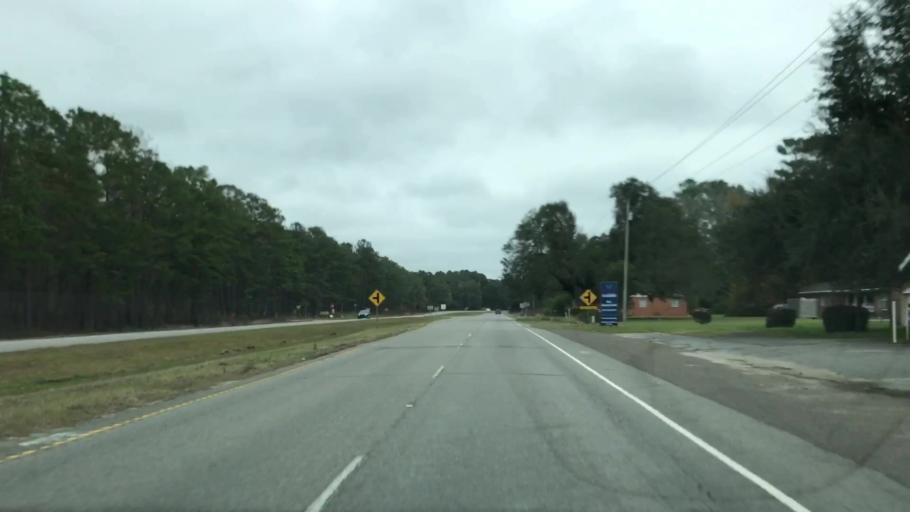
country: US
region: South Carolina
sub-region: Charleston County
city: Awendaw
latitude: 33.0339
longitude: -79.6210
